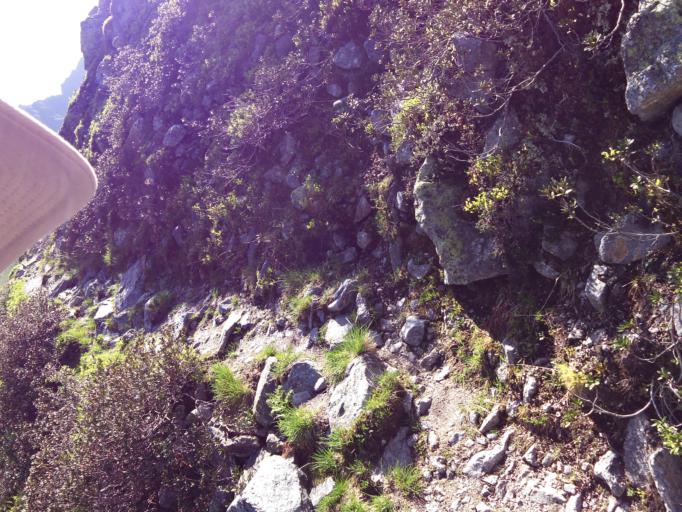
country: AT
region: Tyrol
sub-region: Politischer Bezirk Innsbruck Land
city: Gries im Sellrain
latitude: 47.0826
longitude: 11.1881
